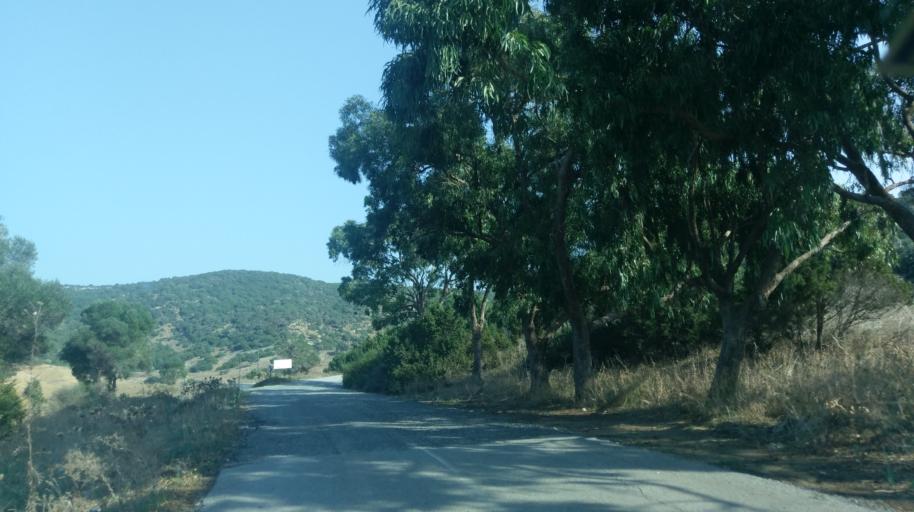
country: CY
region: Ammochostos
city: Rizokarpaso
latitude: 35.6480
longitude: 34.5480
